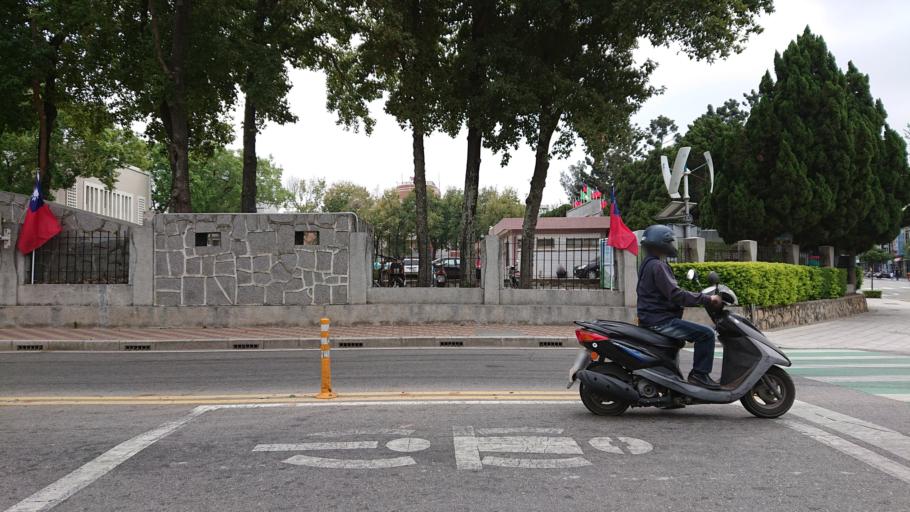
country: TW
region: Fukien
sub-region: Kinmen
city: Jincheng
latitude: 24.4373
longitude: 118.3184
